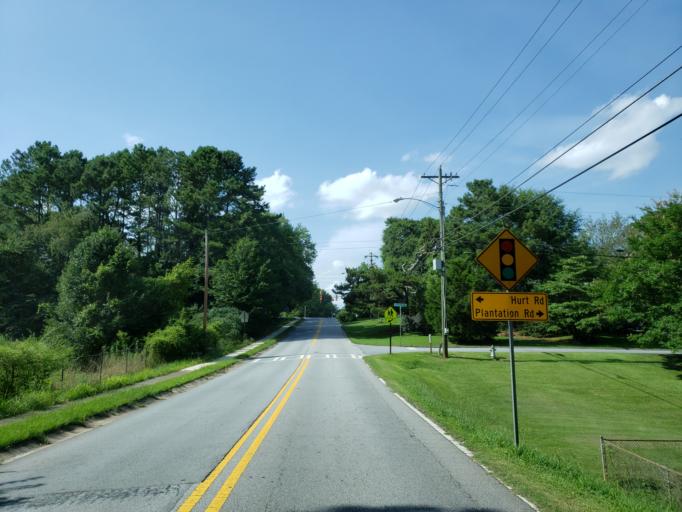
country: US
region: Georgia
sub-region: Cobb County
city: Mableton
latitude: 33.8632
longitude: -84.5690
